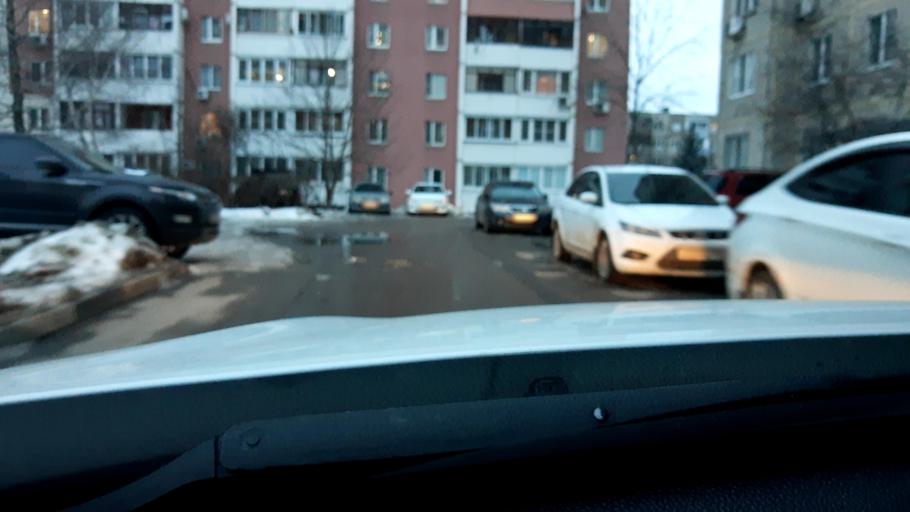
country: RU
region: Moskovskaya
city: Domodedovo
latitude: 55.4540
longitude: 37.7449
